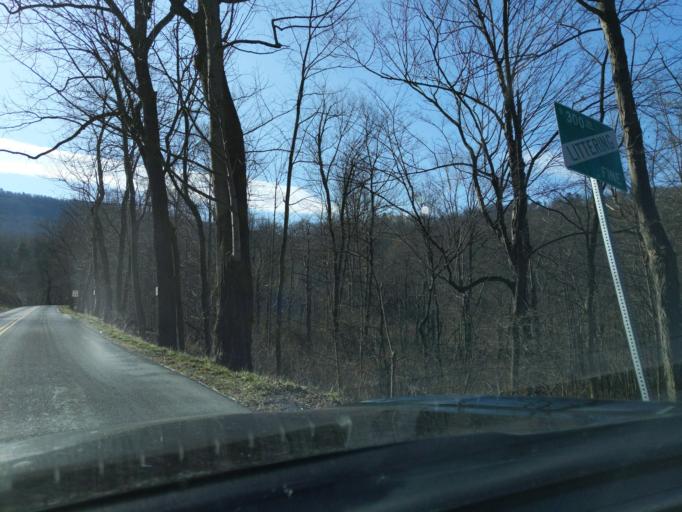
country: US
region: Pennsylvania
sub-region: Blair County
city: Hollidaysburg
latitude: 40.4049
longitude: -78.3195
